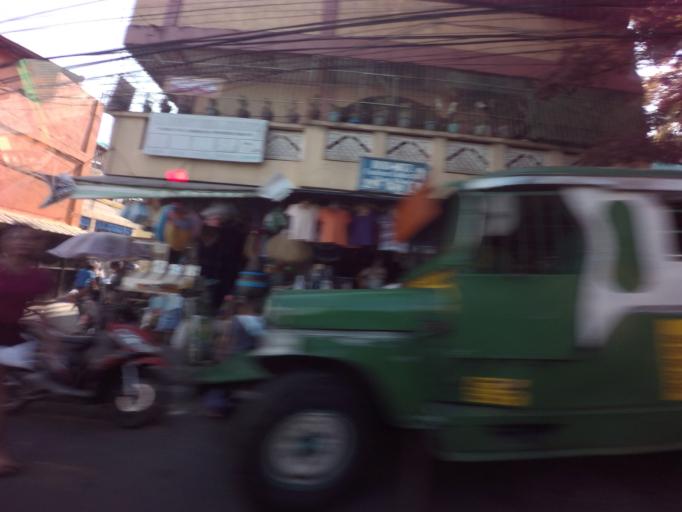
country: PH
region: Calabarzon
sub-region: Province of Rizal
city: Taguig
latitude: 14.5007
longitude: 121.0497
